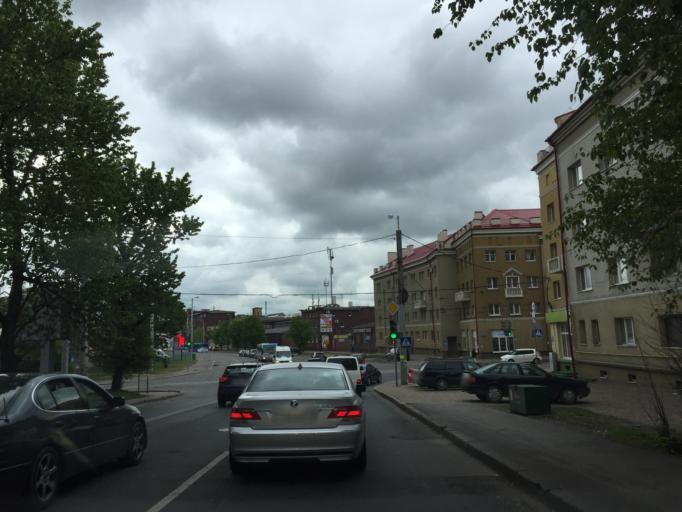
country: RU
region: Kaliningrad
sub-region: Gorod Kaliningrad
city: Kaliningrad
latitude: 54.6974
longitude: 20.4934
